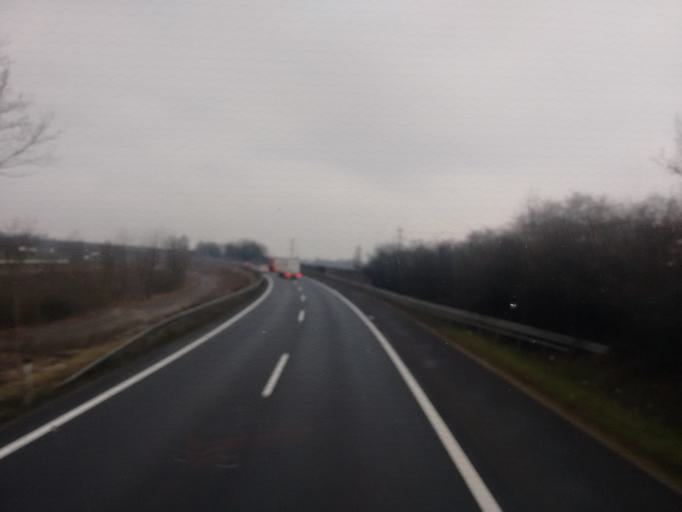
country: AT
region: Upper Austria
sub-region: Wels Stadt
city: Wels
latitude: 48.1814
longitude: 13.9999
